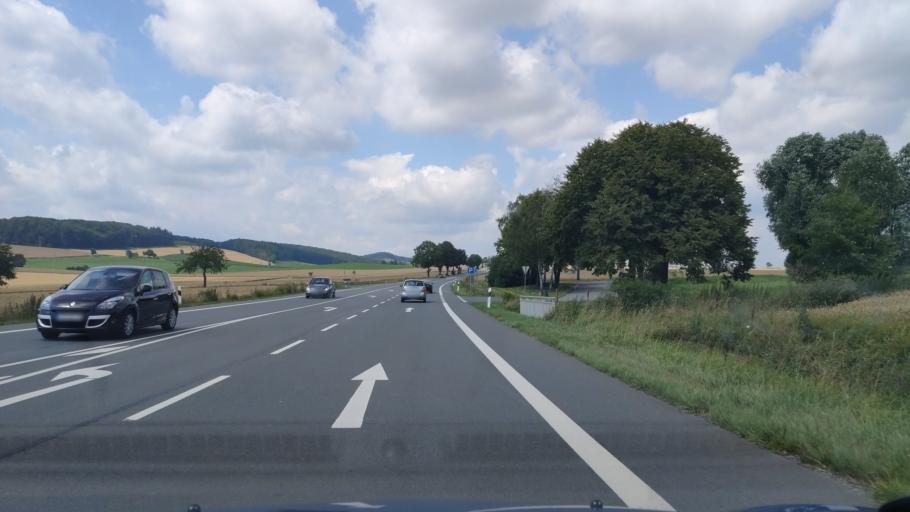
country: DE
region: Lower Saxony
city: Dielmissen
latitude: 51.9717
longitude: 9.5919
